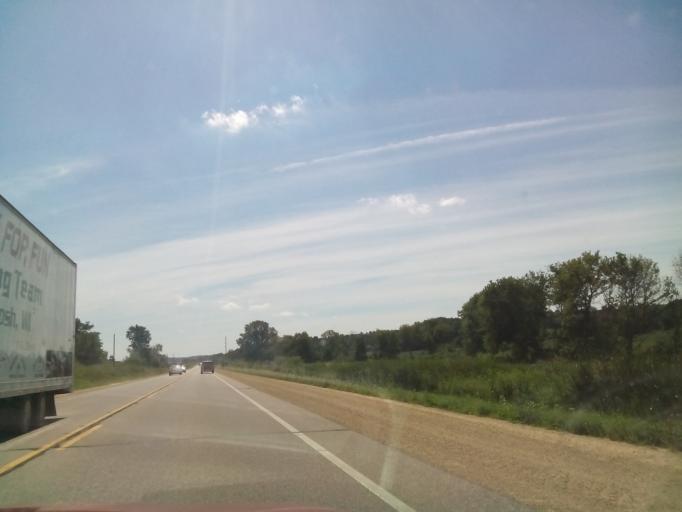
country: US
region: Wisconsin
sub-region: Green County
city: Monticello
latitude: 42.7695
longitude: -89.6256
